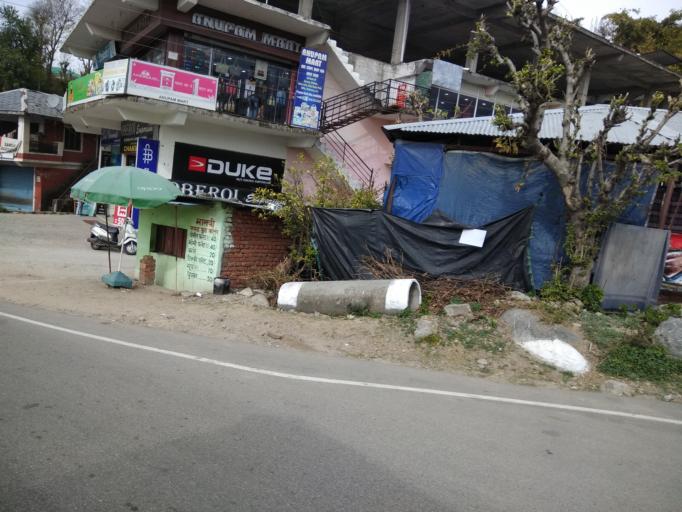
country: IN
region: Himachal Pradesh
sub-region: Kangra
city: Dharmsala
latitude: 32.1980
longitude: 76.3436
